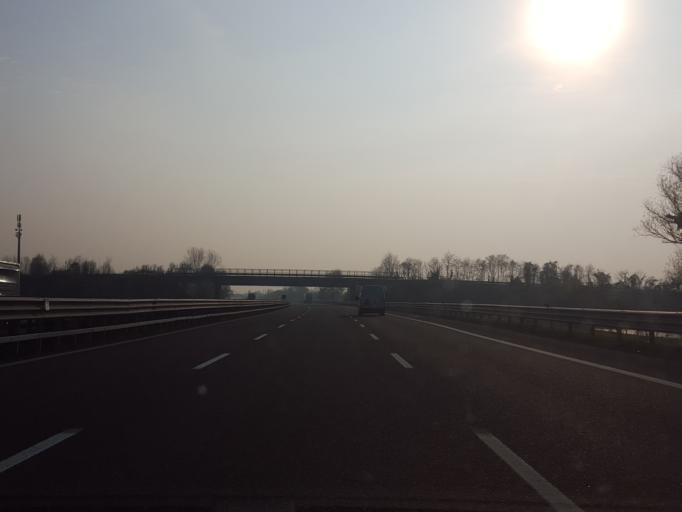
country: IT
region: Veneto
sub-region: Provincia di Treviso
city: Conscio
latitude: 45.6155
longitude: 12.2997
